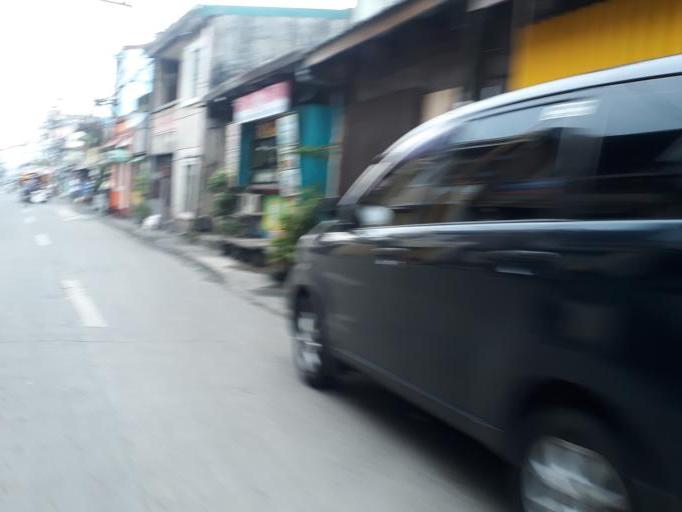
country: PH
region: Calabarzon
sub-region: Province of Rizal
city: Malabon
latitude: 14.6697
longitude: 120.9391
